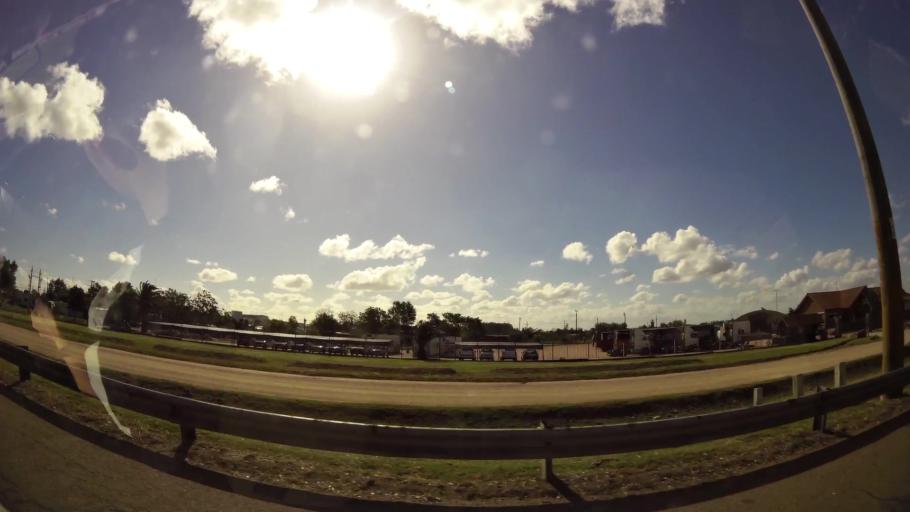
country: UY
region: Canelones
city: La Paz
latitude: -34.8326
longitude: -56.2536
